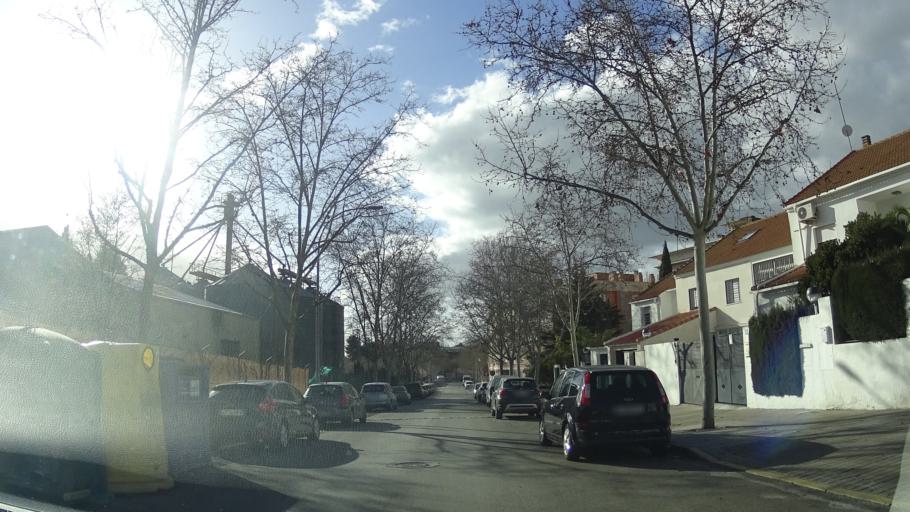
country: ES
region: Castille-La Mancha
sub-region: Provincia de Ciudad Real
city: Ciudad Real
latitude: 38.9780
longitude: -3.9326
